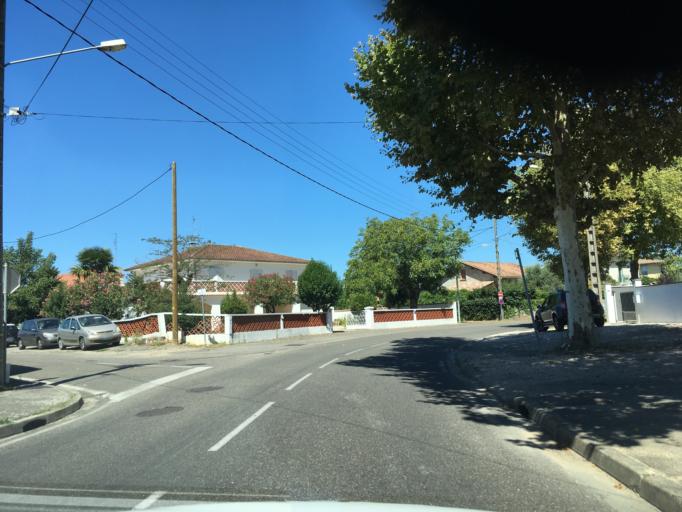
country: FR
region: Midi-Pyrenees
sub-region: Departement du Tarn-et-Garonne
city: Montauban
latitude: 44.0280
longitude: 1.3539
